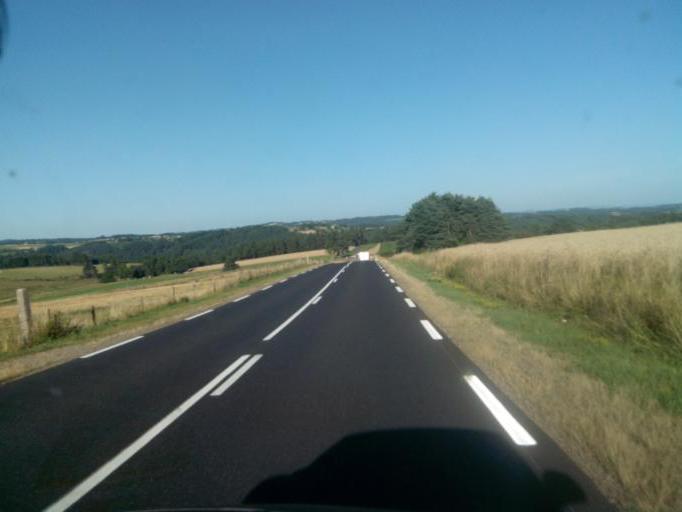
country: FR
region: Auvergne
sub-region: Departement de la Haute-Loire
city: Craponne-sur-Arzon
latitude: 45.3437
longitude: 3.8801
